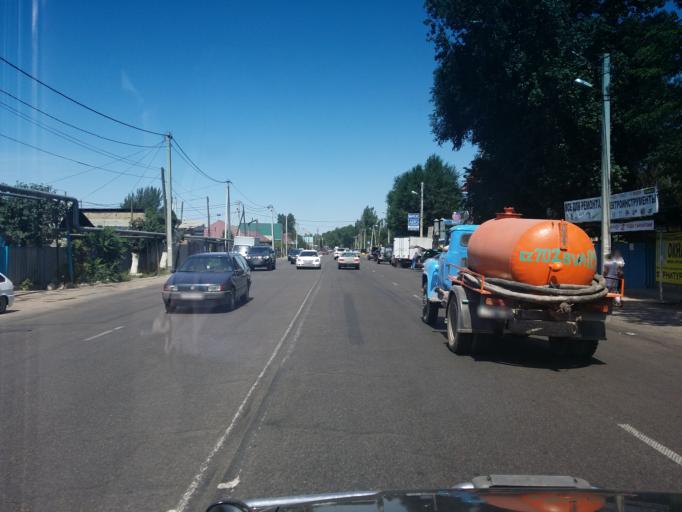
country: KZ
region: Almaty Oblysy
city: Pervomayskiy
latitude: 43.3266
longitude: 76.9318
